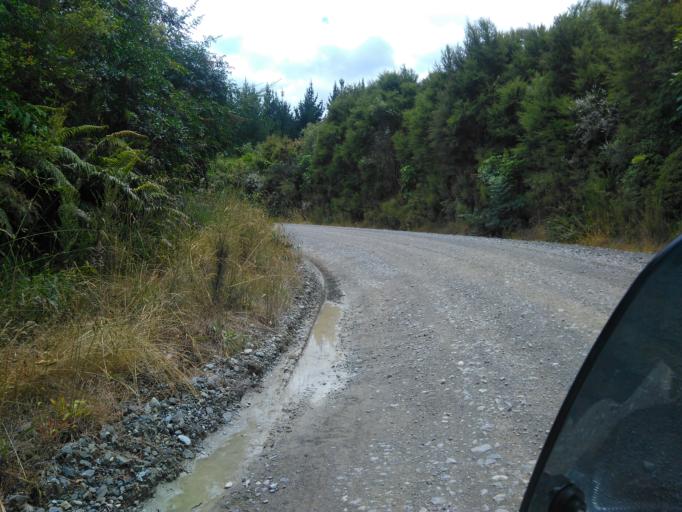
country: NZ
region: Gisborne
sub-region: Gisborne District
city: Gisborne
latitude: -38.1658
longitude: 178.1366
